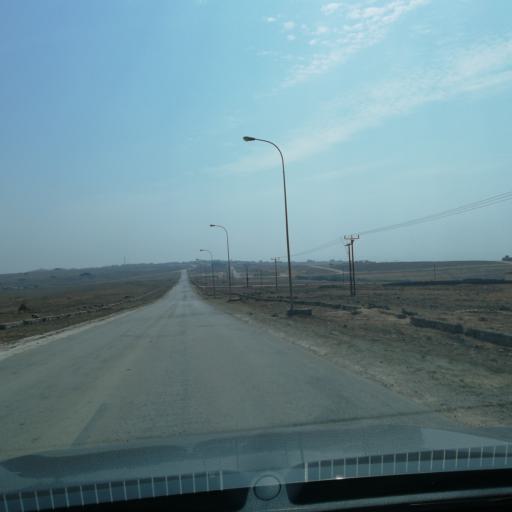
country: OM
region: Zufar
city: Salalah
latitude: 17.2402
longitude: 54.0591
